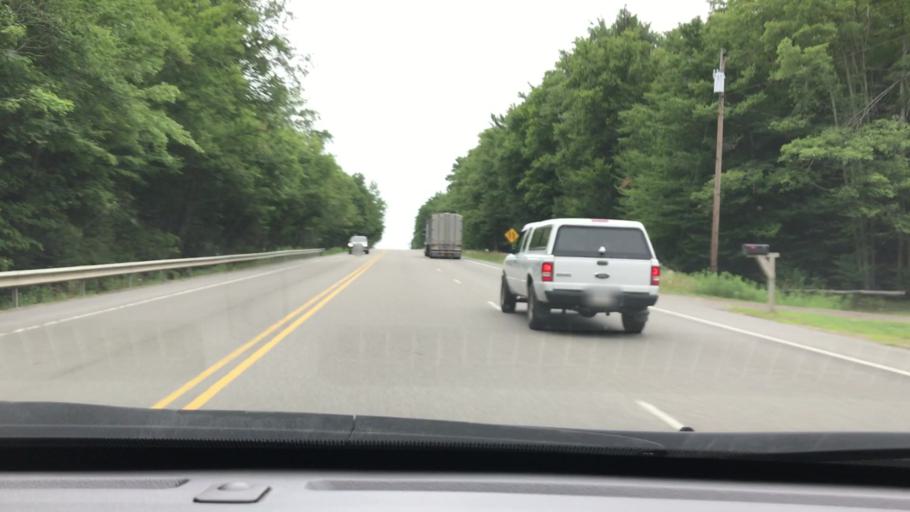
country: US
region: Pennsylvania
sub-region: McKean County
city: Kane
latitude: 41.7020
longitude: -78.6923
